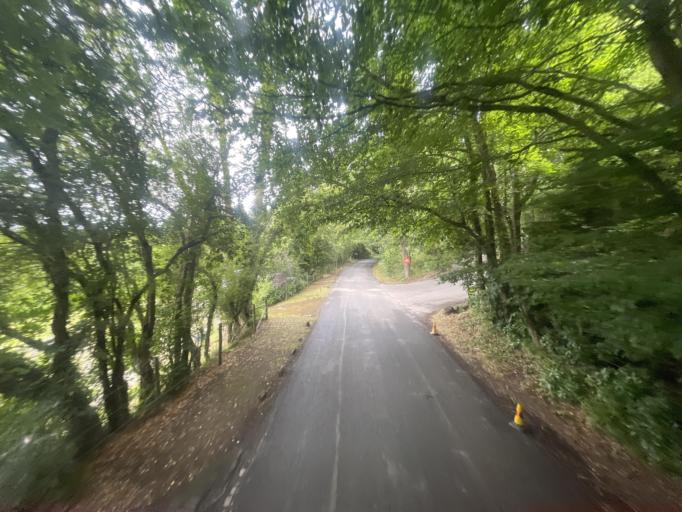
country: GB
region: England
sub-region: Kent
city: Edenbridge
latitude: 51.1630
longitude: 0.1616
